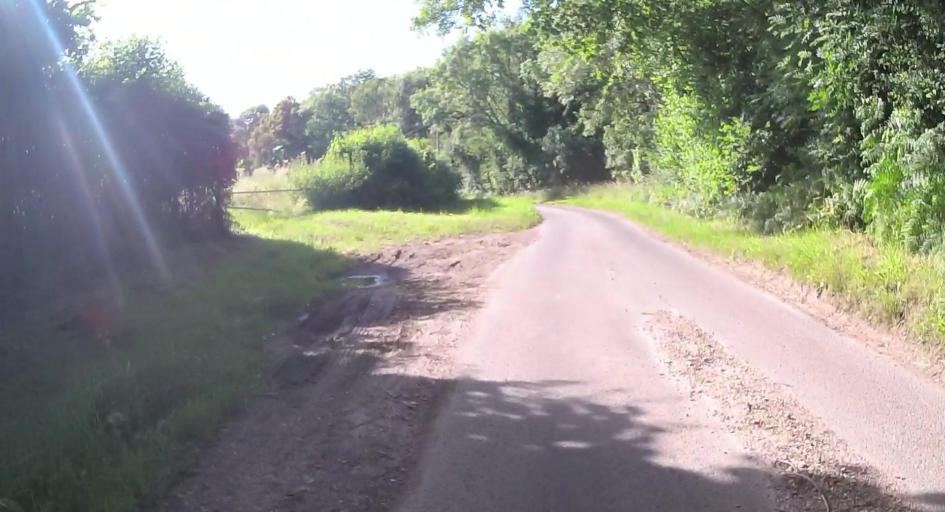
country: GB
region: England
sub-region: Hampshire
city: Long Sutton
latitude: 51.1898
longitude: -0.9521
